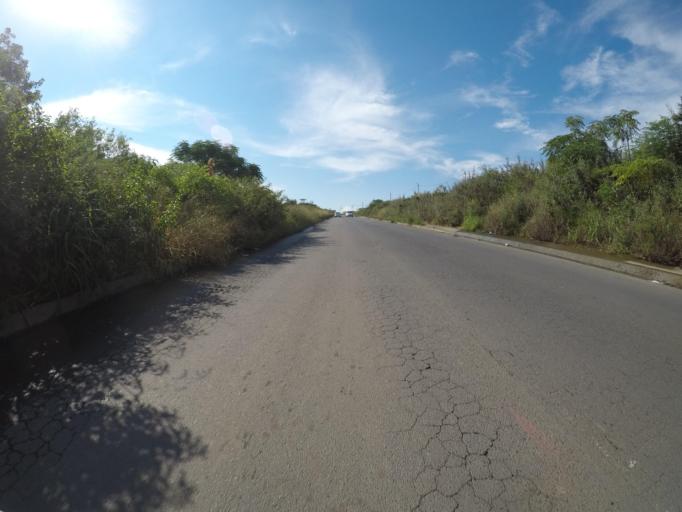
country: ZA
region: Eastern Cape
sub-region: Buffalo City Metropolitan Municipality
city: East London
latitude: -33.0089
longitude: 27.8580
